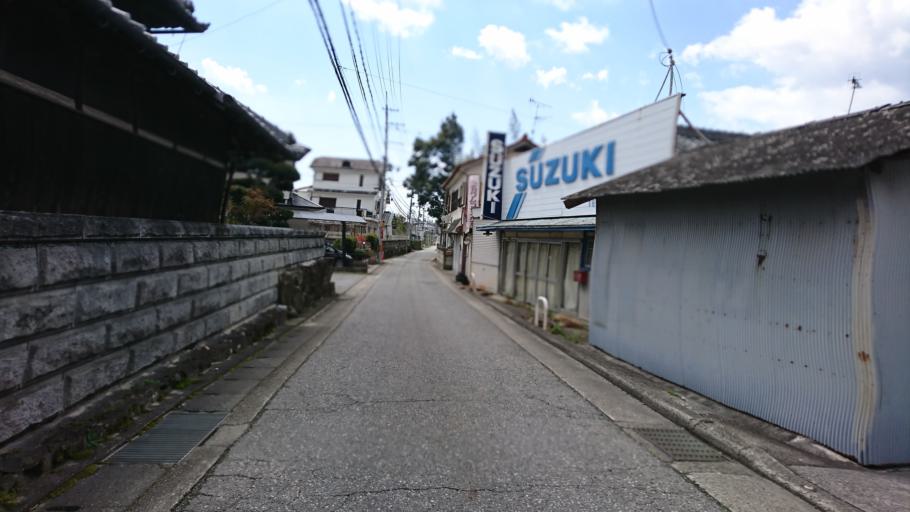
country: JP
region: Hyogo
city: Miki
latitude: 34.7659
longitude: 134.9579
